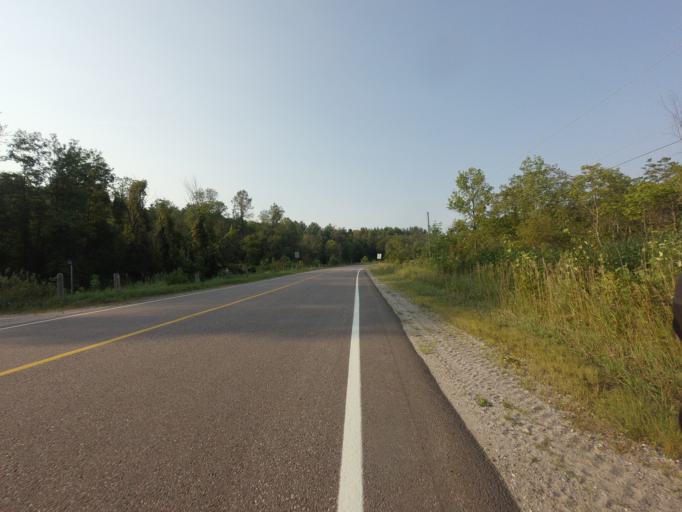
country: CA
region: Ontario
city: Perth
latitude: 44.9426
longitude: -76.6869
